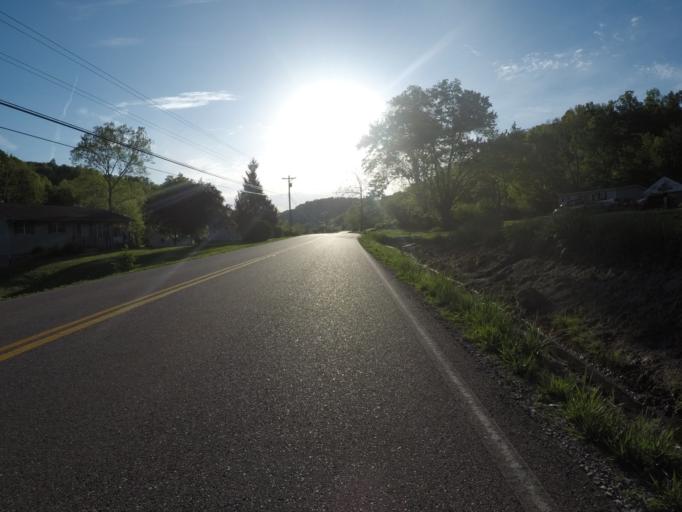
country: US
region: West Virginia
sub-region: Cabell County
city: Huntington
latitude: 38.5544
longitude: -82.4472
